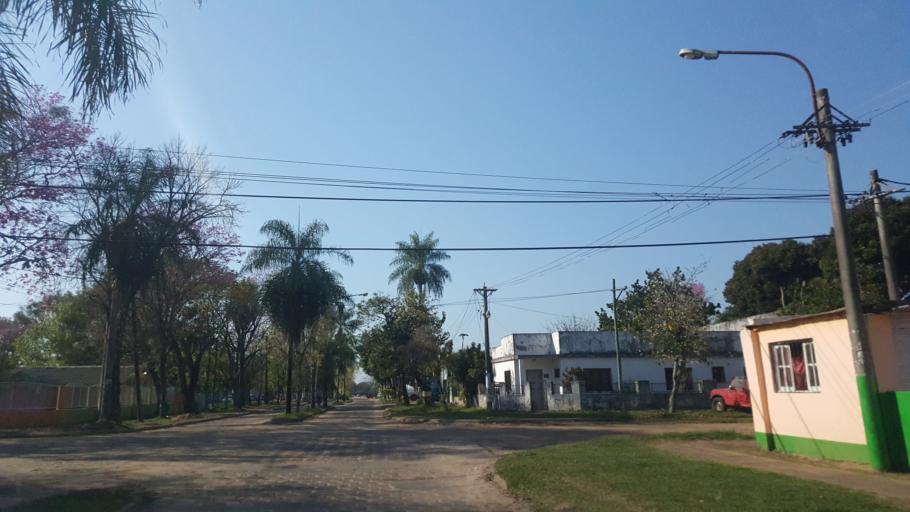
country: AR
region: Corrientes
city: Ituzaingo
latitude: -27.5916
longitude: -56.6881
